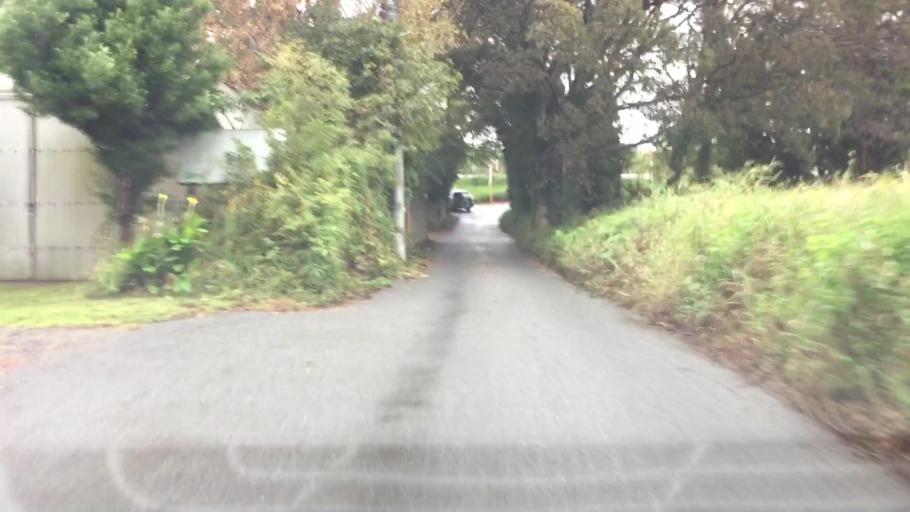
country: JP
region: Ibaraki
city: Toride
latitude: 35.8692
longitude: 140.1187
